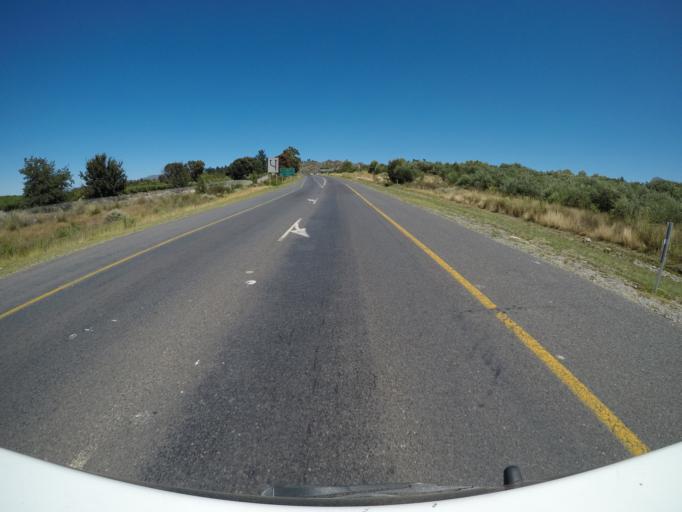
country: ZA
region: Western Cape
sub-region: Overberg District Municipality
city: Grabouw
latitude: -34.1623
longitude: 19.0133
